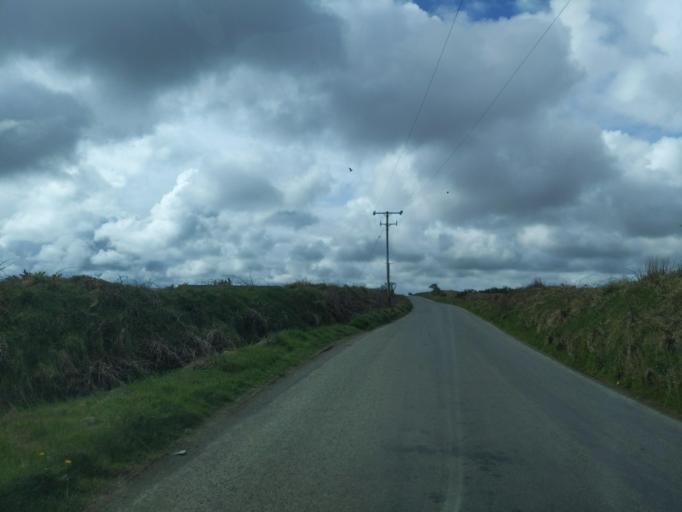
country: GB
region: England
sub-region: Cornwall
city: Camelford
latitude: 50.6409
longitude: -4.6385
